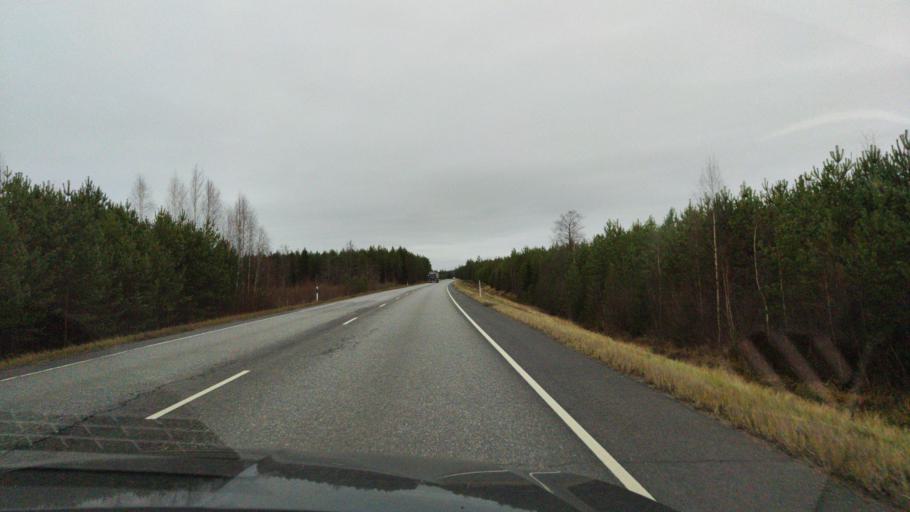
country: FI
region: Varsinais-Suomi
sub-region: Loimaa
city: Ylaene
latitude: 60.9757
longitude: 22.4097
